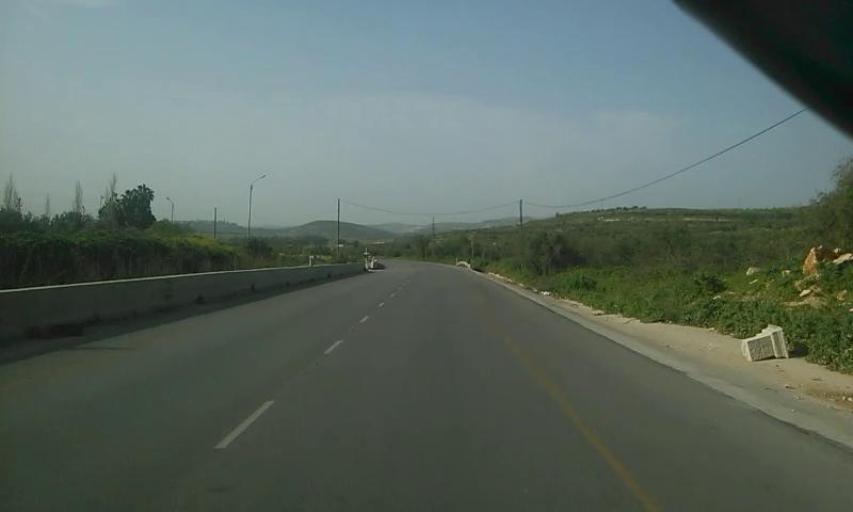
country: PS
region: West Bank
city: Dayr Sharaf
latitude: 32.2586
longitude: 35.1764
